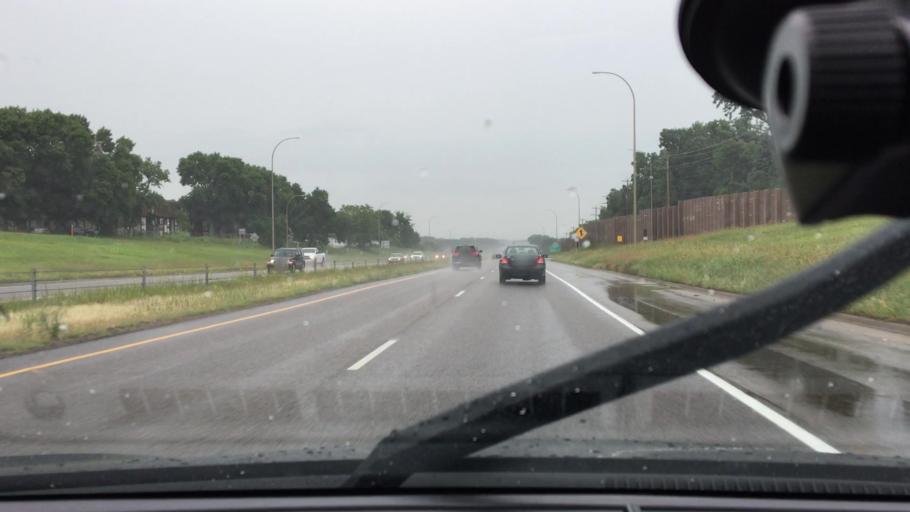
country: US
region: Minnesota
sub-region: Hennepin County
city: New Hope
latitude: 45.0225
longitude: -93.4007
